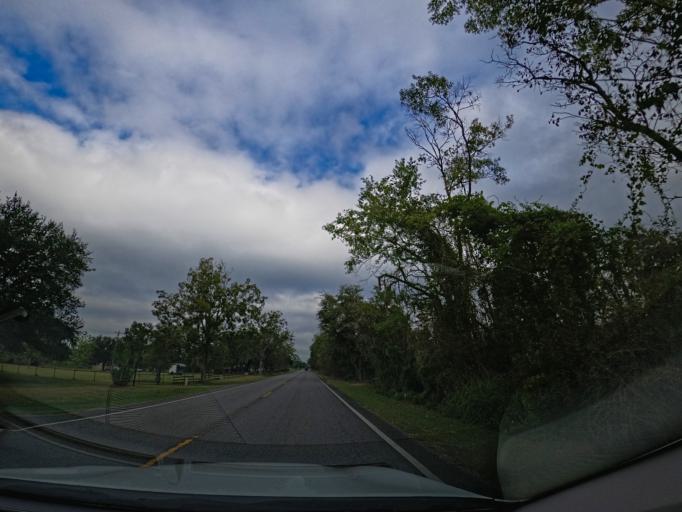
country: US
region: Louisiana
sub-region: Saint Mary Parish
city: Amelia
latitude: 29.6517
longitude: -90.9701
